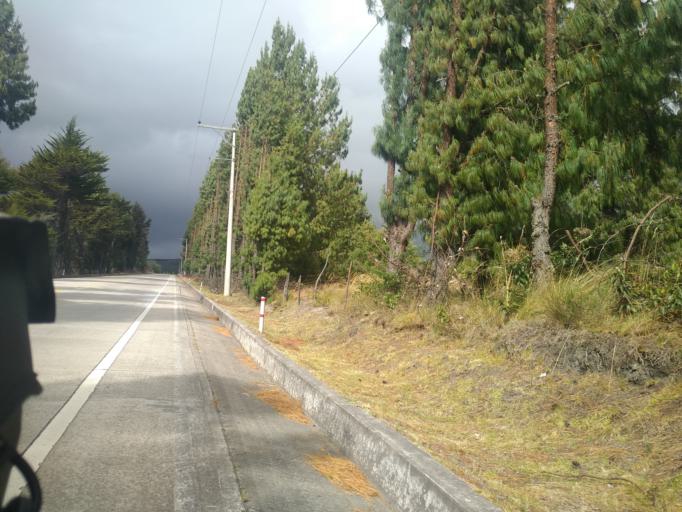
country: EC
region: Azuay
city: Cuenca
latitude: -3.3520
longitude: -79.1860
